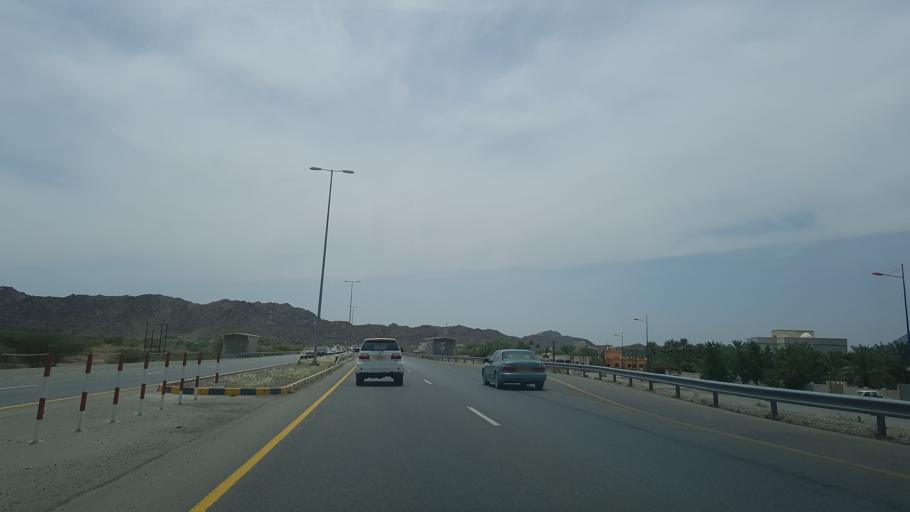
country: OM
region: Muhafazat ad Dakhiliyah
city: Izki
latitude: 22.9944
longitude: 57.7912
